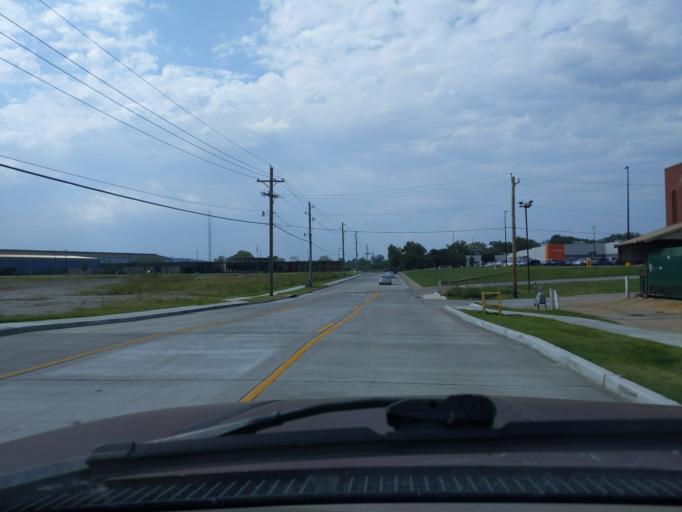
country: US
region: Oklahoma
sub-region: Tulsa County
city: Sand Springs
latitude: 36.1337
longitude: -96.1174
